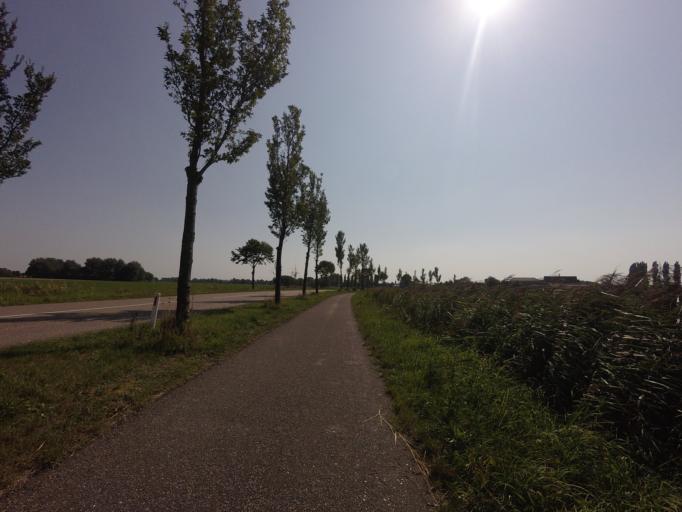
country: NL
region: Groningen
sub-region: Gemeente Zuidhorn
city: Grijpskerk
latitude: 53.2705
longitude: 6.3074
